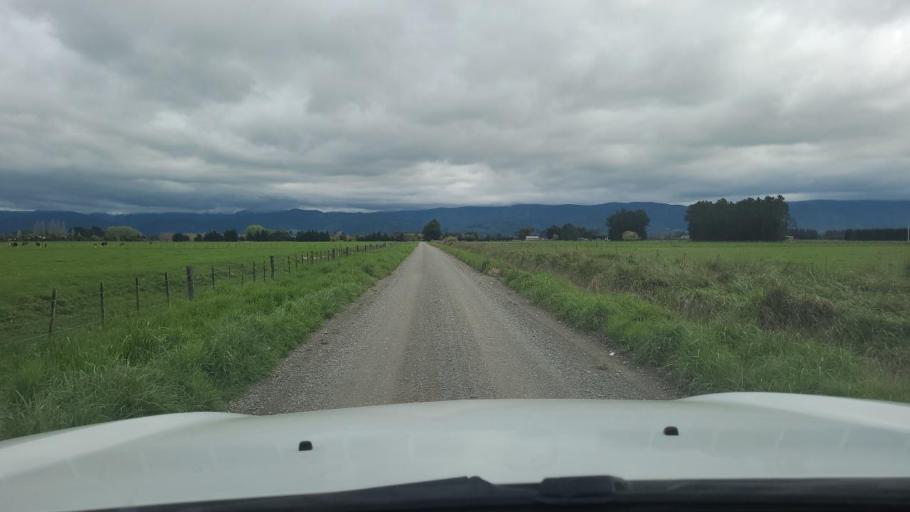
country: NZ
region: Wellington
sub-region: South Wairarapa District
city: Waipawa
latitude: -41.1458
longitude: 175.4022
